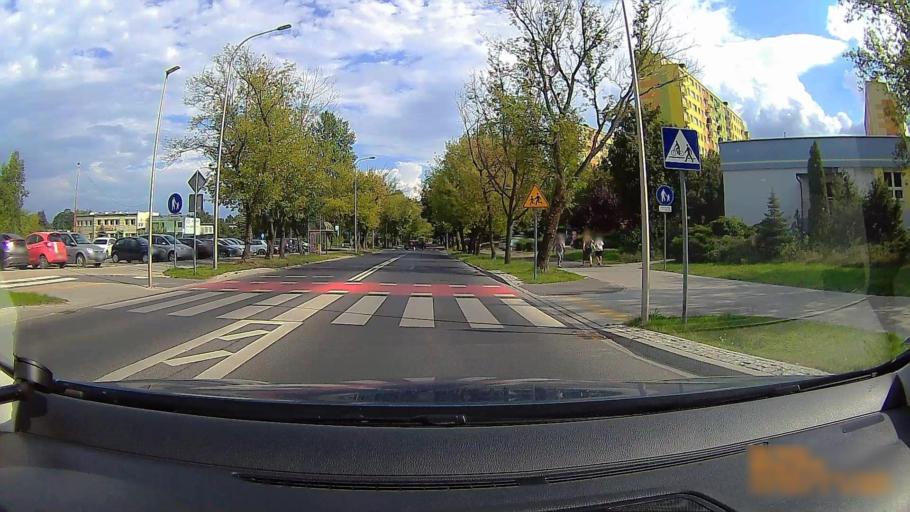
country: PL
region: Greater Poland Voivodeship
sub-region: Konin
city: Konin
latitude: 52.2315
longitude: 18.2785
